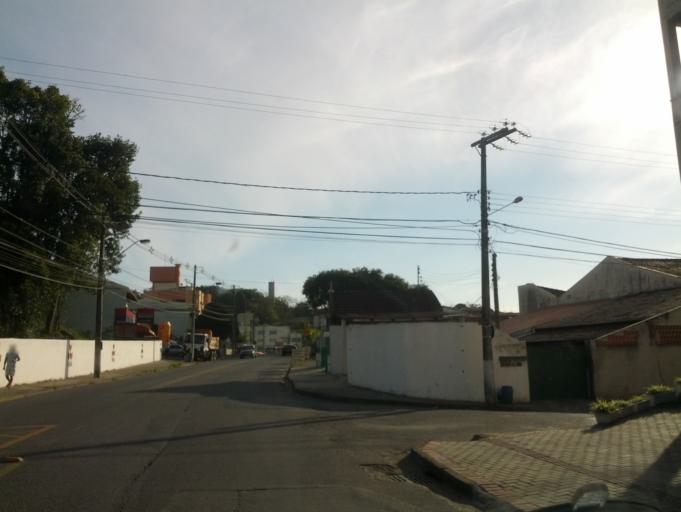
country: BR
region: Santa Catarina
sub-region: Blumenau
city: Blumenau
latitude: -26.9089
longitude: -49.1240
